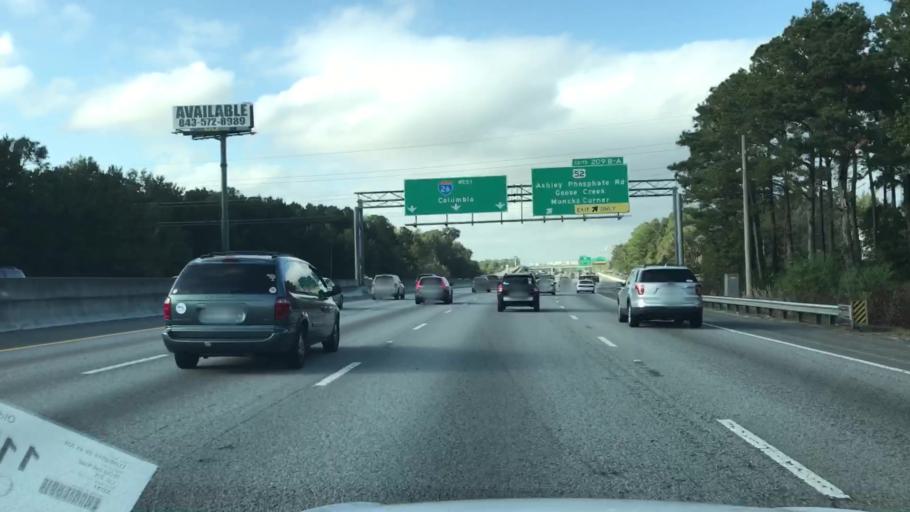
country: US
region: South Carolina
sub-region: Berkeley County
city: Hanahan
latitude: 32.9280
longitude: -80.0437
